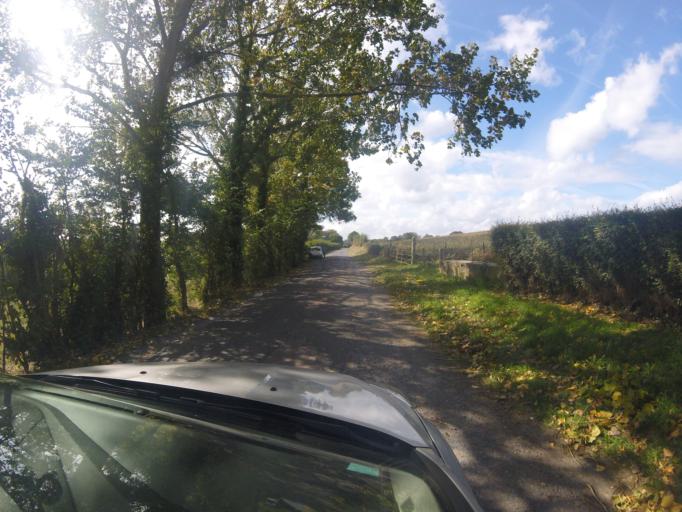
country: FR
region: Lower Normandy
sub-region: Departement du Calvados
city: Saint-Vigor-le-Grand
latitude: 49.3203
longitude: -0.6394
